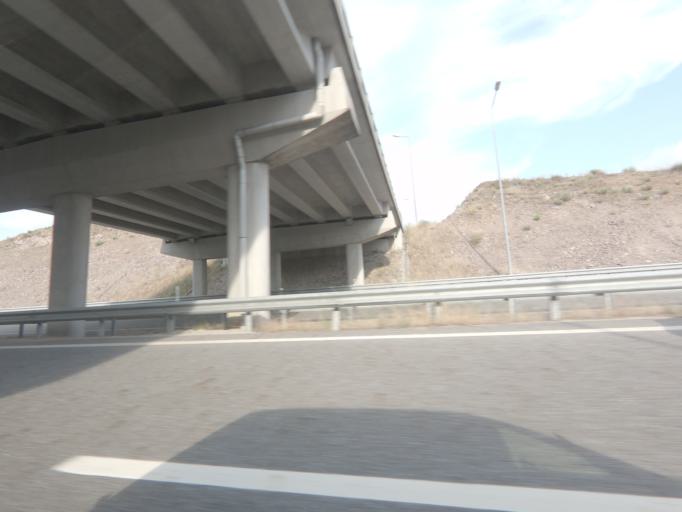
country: PT
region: Vila Real
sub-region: Boticas
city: Boticas
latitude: 41.6486
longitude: -7.5822
